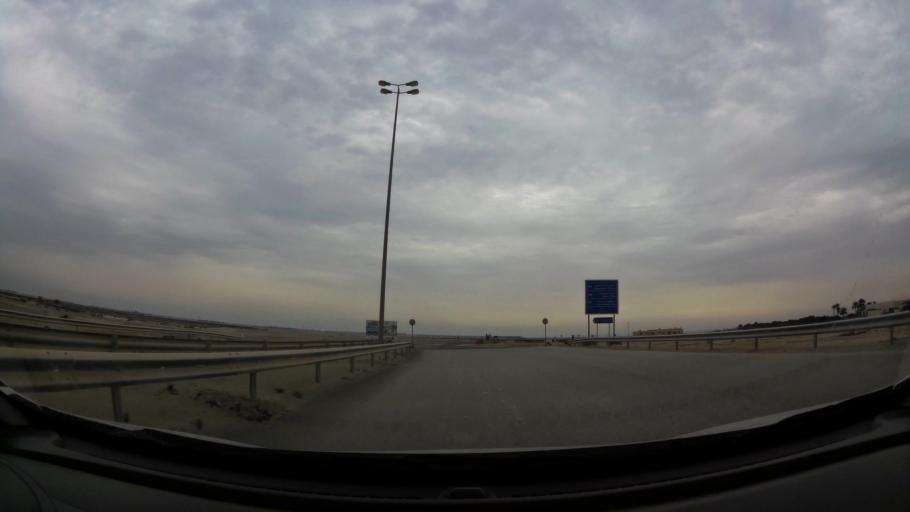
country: BH
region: Central Governorate
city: Dar Kulayb
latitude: 25.8395
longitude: 50.5868
